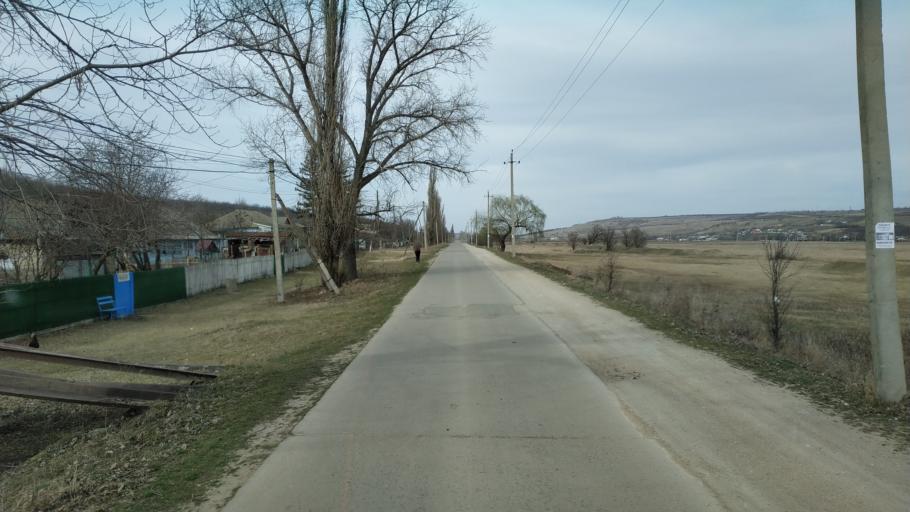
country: RO
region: Vaslui
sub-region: Comuna Dranceni
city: Dranceni
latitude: 46.8632
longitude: 28.2013
